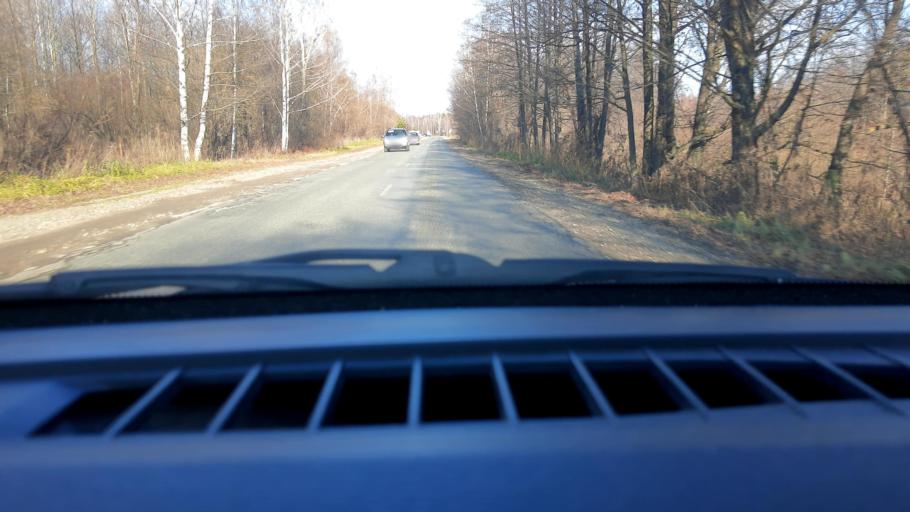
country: RU
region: Nizjnij Novgorod
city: Neklyudovo
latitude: 56.4325
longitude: 43.9225
